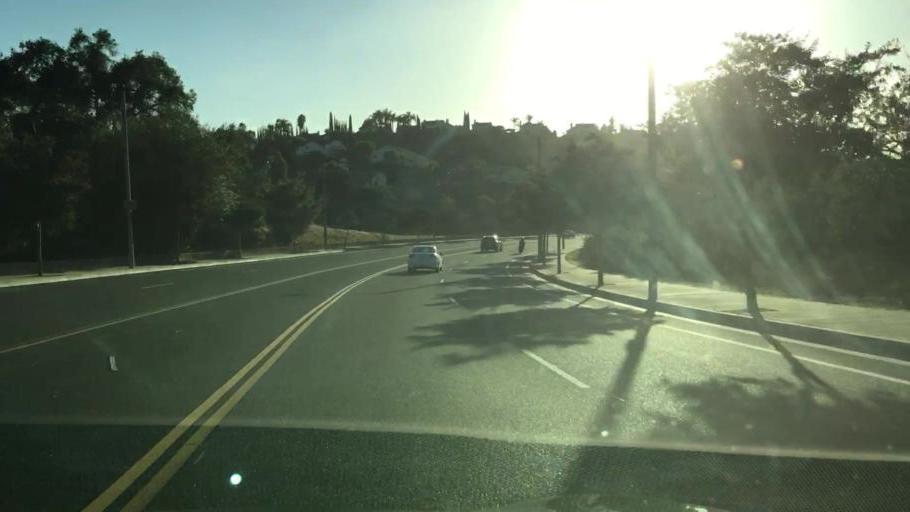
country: US
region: California
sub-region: Los Angeles County
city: Rowland Heights
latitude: 33.9718
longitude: -117.8647
